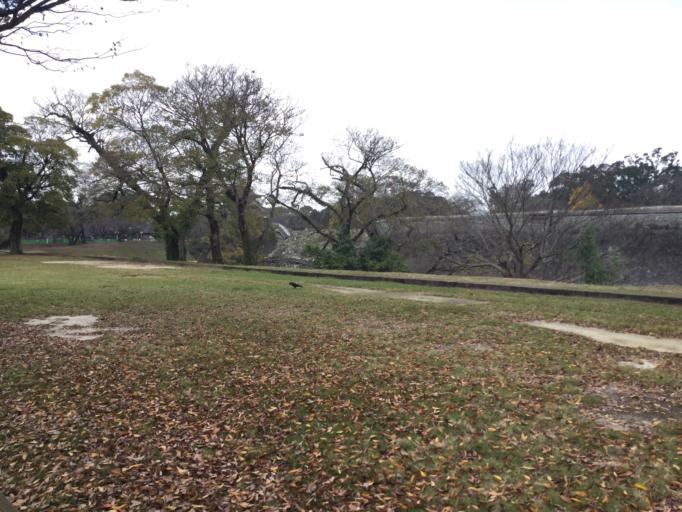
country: JP
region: Kumamoto
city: Kumamoto
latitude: 32.8062
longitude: 130.7026
